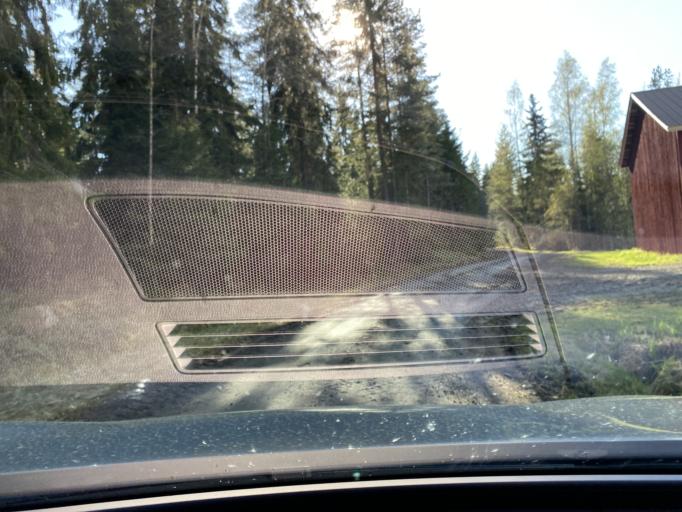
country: FI
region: Pirkanmaa
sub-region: Lounais-Pirkanmaa
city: Punkalaidun
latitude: 61.0196
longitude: 23.2085
